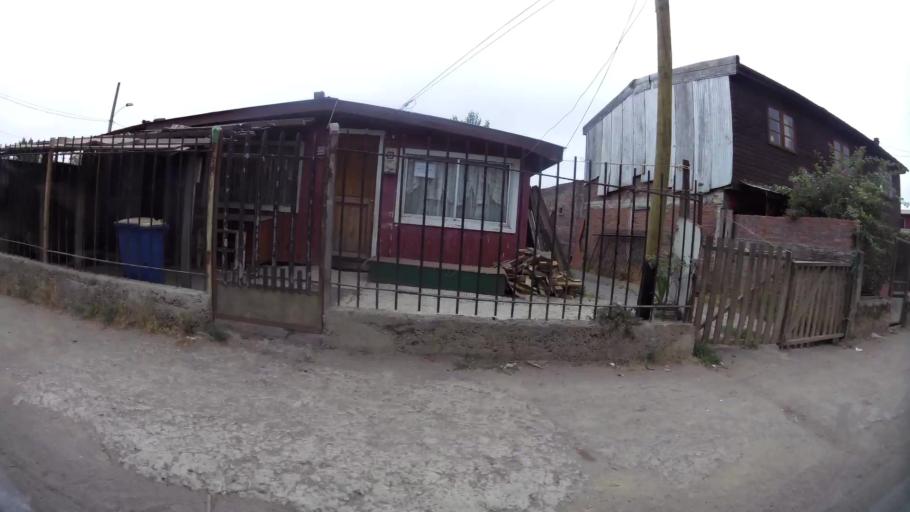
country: CL
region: Biobio
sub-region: Provincia de Concepcion
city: Concepcion
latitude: -36.8200
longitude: -72.9887
